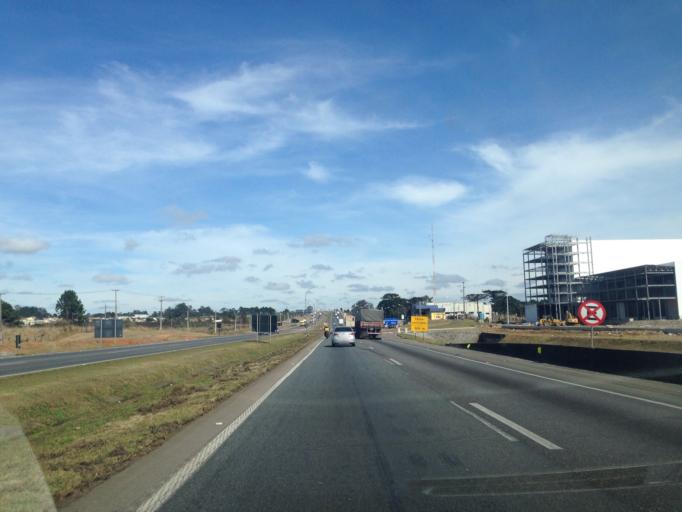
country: BR
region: Parana
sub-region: Sao Jose Dos Pinhais
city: Sao Jose dos Pinhais
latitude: -25.5251
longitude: -49.1388
